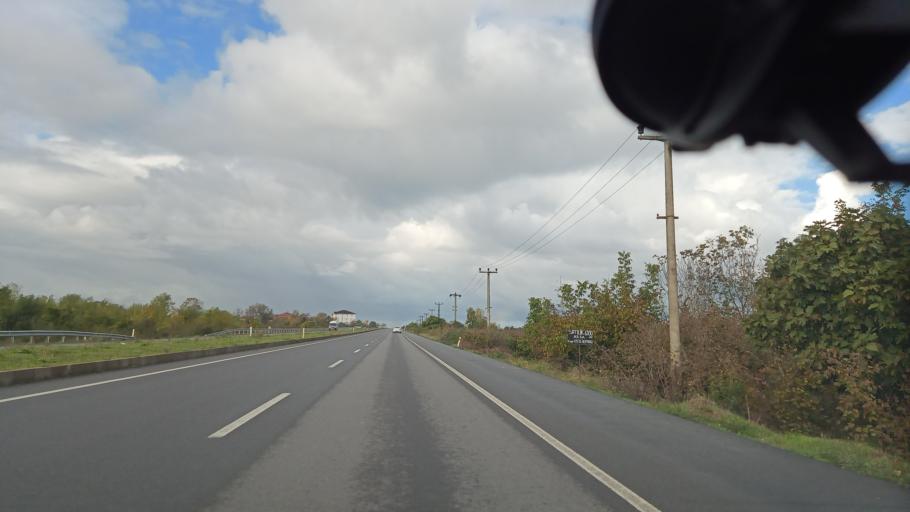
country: TR
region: Sakarya
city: Karasu
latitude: 41.0718
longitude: 30.7928
